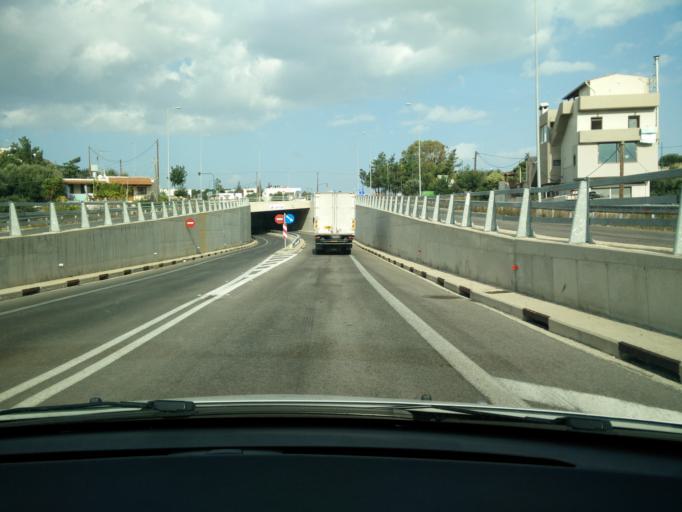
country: GR
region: Crete
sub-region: Nomos Lasithiou
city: Agios Nikolaos
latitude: 35.1835
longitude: 25.7043
